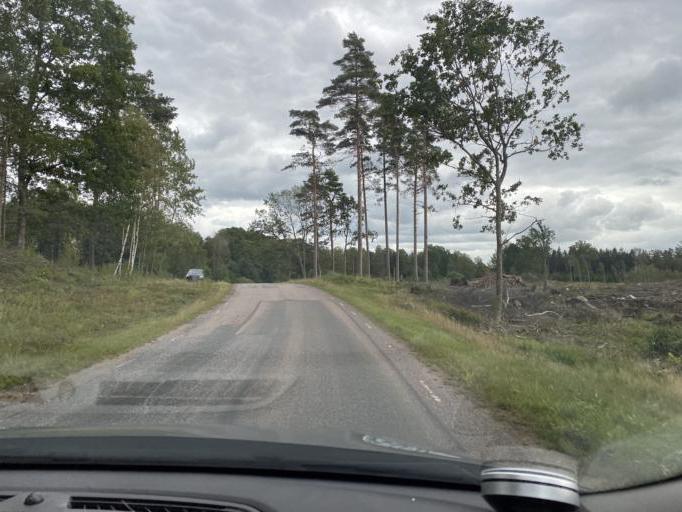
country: SE
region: Kronoberg
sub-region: Markaryds Kommun
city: Markaryd
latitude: 56.4877
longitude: 13.5539
